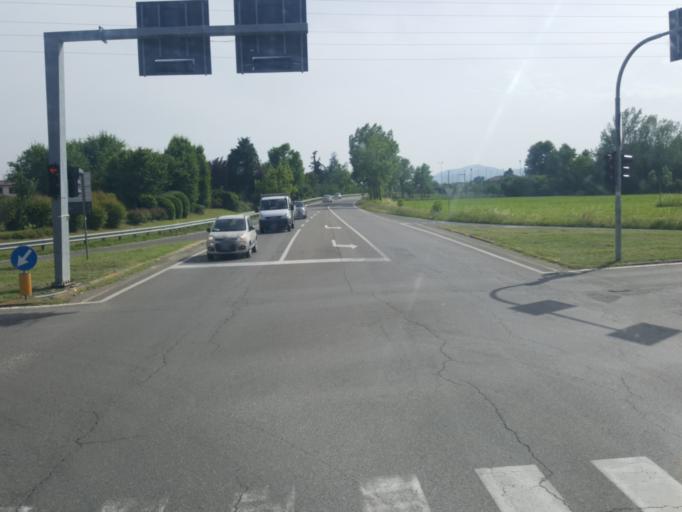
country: IT
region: Emilia-Romagna
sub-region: Provincia di Piacenza
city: Niviano
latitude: 44.9417
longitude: 9.6328
